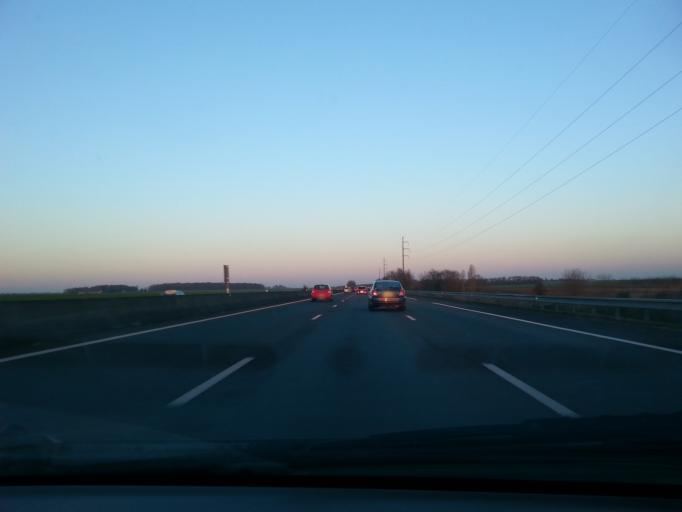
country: FR
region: Centre
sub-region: Departement d'Eure-et-Loir
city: Bailleau-le-Pin
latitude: 48.3034
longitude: 1.2968
